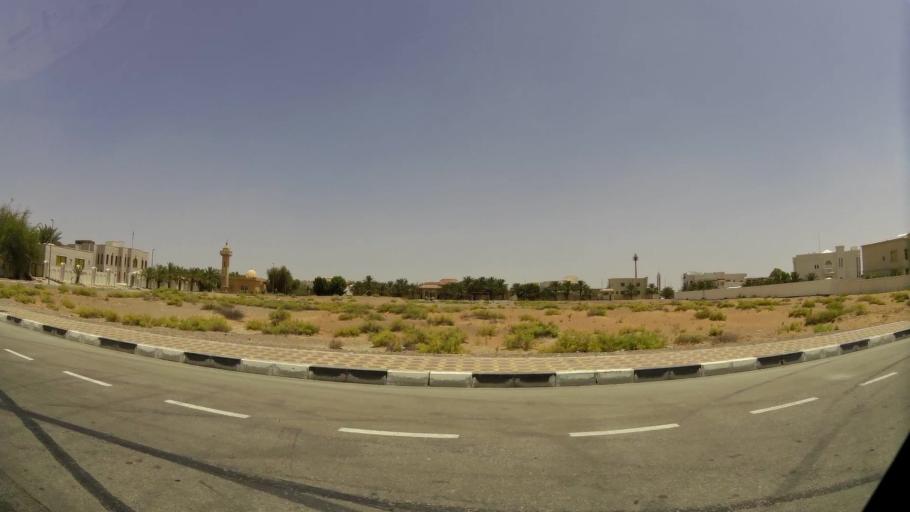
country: OM
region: Al Buraimi
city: Al Buraymi
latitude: 24.2653
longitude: 55.7127
